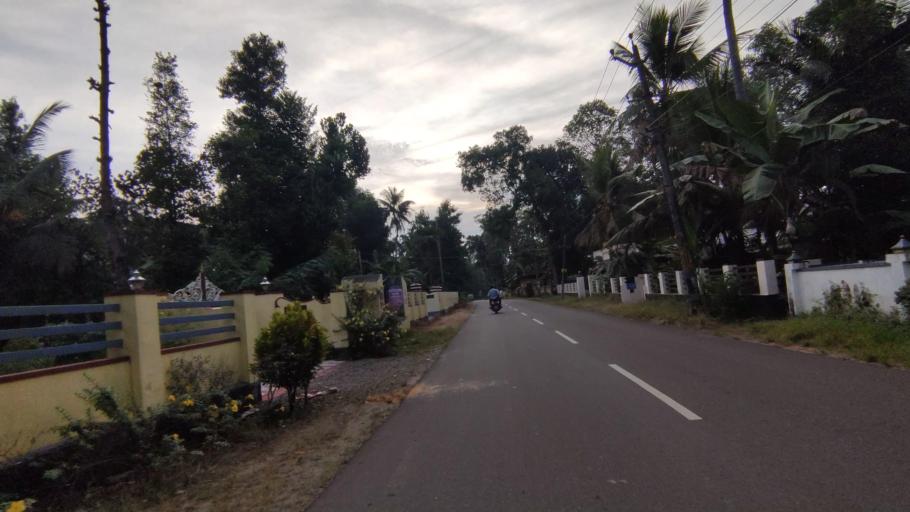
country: IN
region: Kerala
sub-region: Kottayam
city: Kottayam
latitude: 9.6372
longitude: 76.4954
